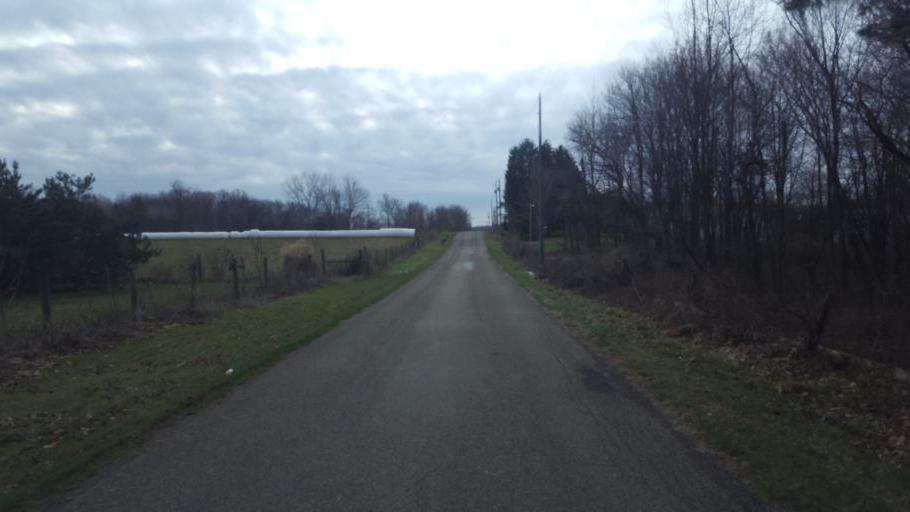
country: US
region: Ohio
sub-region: Knox County
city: Fredericktown
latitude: 40.5057
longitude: -82.4714
